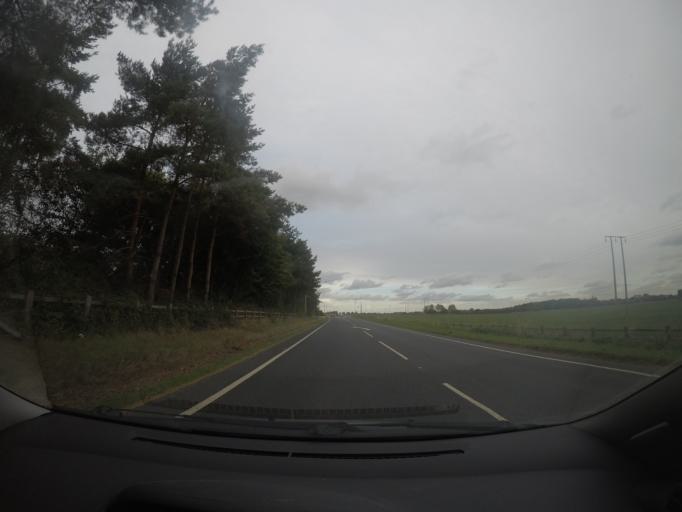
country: GB
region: England
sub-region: North Yorkshire
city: Barlby
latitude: 53.8077
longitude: -1.0375
